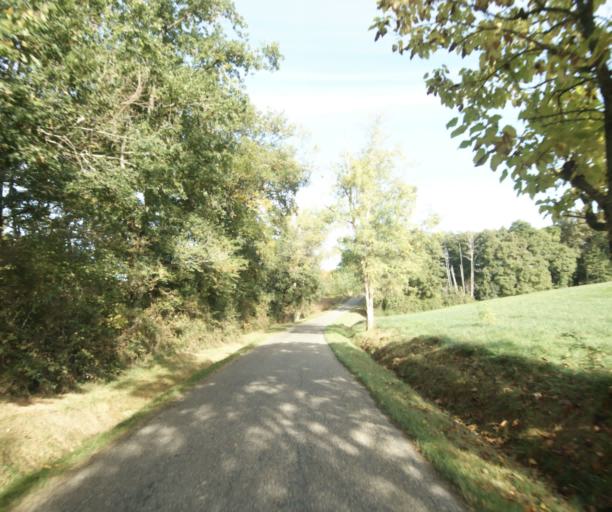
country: FR
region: Midi-Pyrenees
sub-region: Departement du Gers
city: Eauze
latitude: 43.9284
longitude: 0.1242
